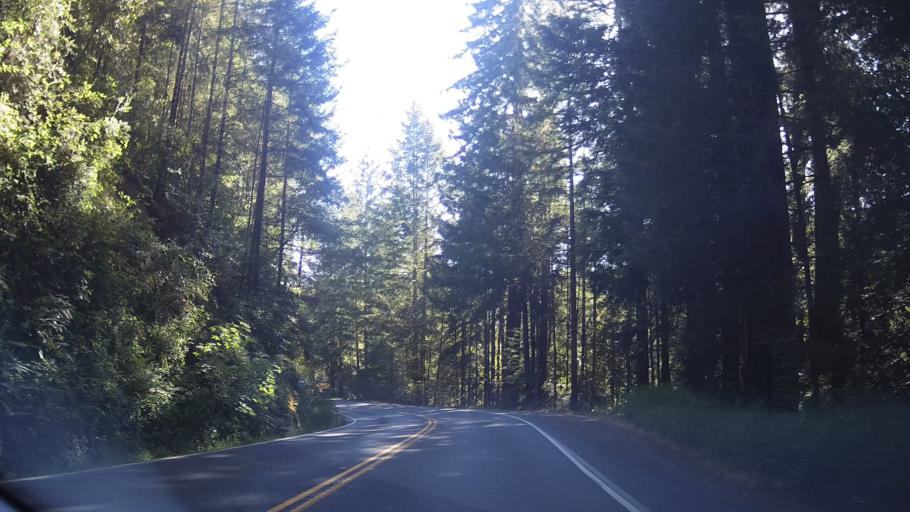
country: US
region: California
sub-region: Mendocino County
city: Brooktrails
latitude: 39.3683
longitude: -123.4972
